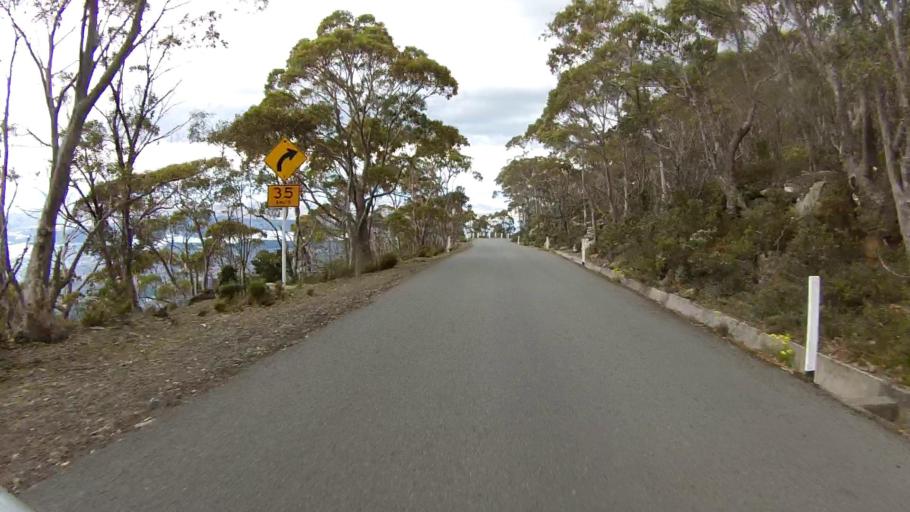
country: AU
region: Tasmania
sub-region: Glenorchy
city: West Moonah
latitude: -42.8878
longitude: 147.2270
